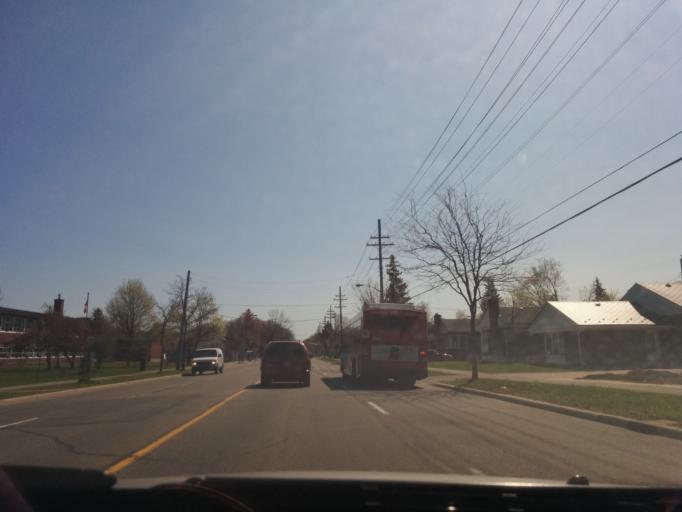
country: CA
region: Ontario
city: Ottawa
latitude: 45.4001
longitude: -75.6372
